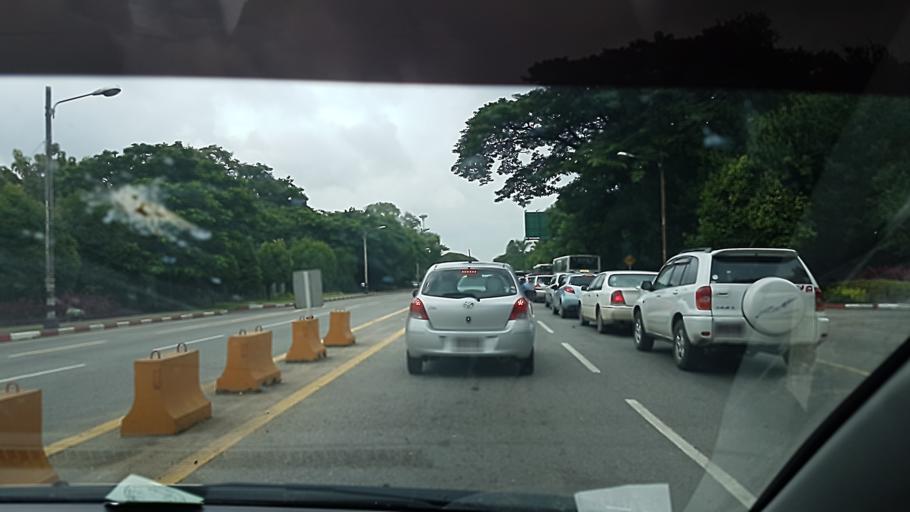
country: MM
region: Yangon
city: Yangon
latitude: 16.7949
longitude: 96.1398
